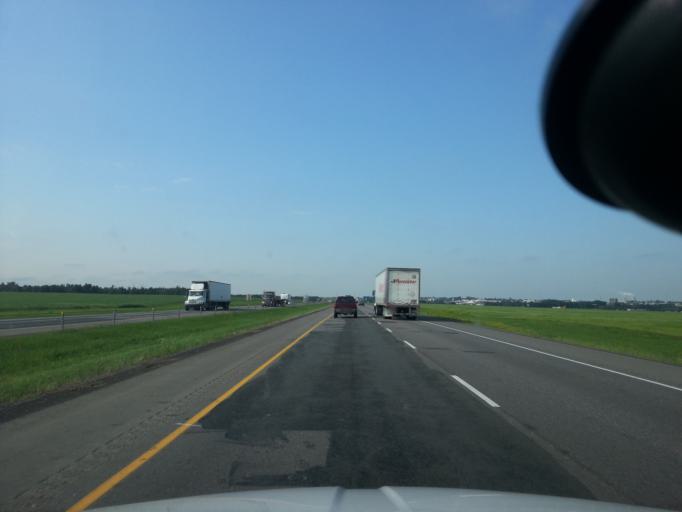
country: CA
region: Alberta
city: Penhold
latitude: 52.0408
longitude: -113.9127
